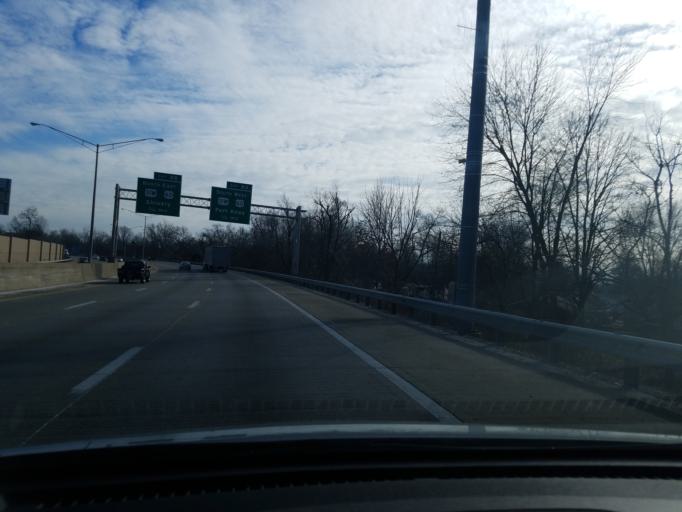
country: US
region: Kentucky
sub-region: Jefferson County
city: Shively
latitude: 38.1882
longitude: -85.8296
